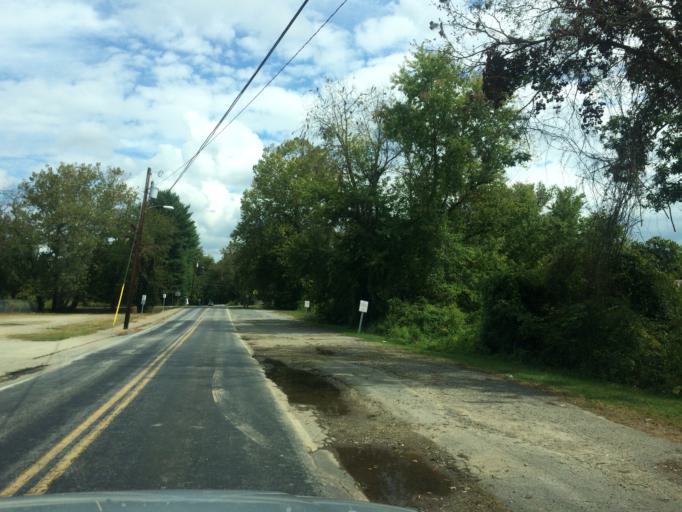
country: US
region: North Carolina
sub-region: Haywood County
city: Clyde
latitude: 35.5355
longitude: -82.9135
